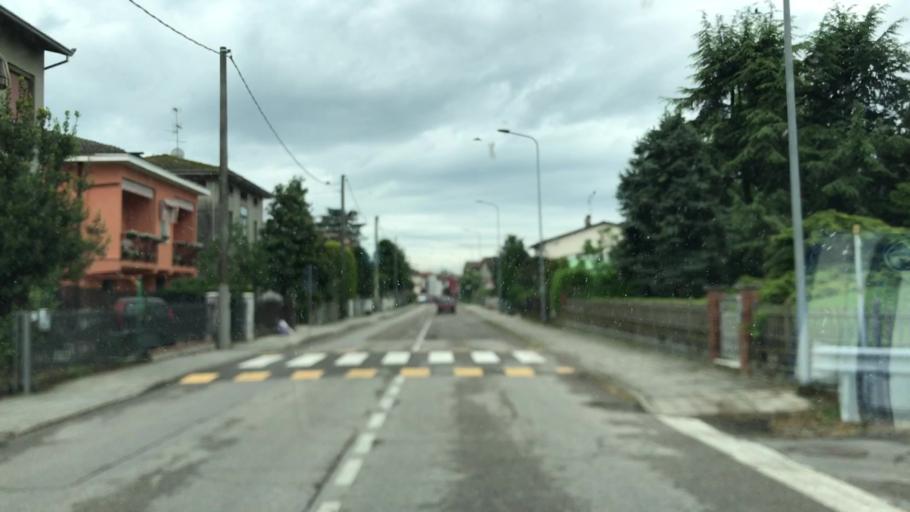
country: IT
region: Lombardy
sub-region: Provincia di Mantova
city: San Giovanni del Dosso
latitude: 44.9704
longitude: 11.0829
